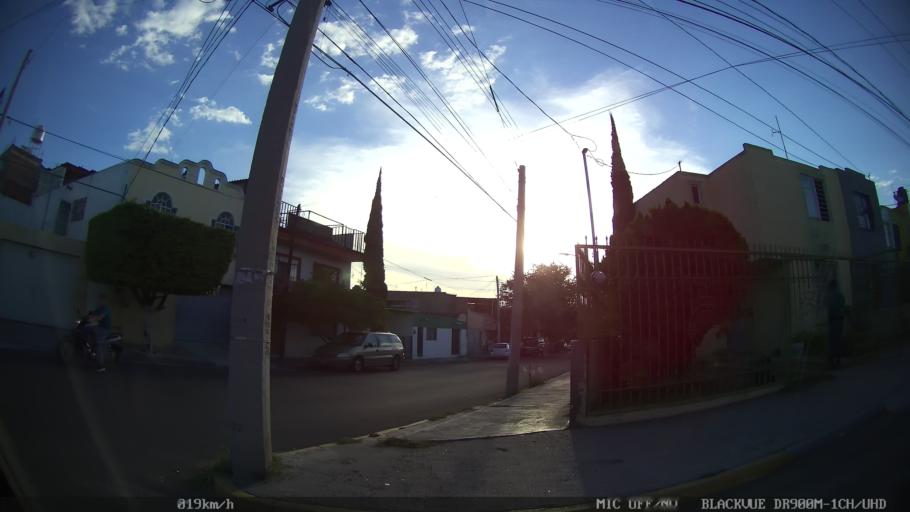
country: MX
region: Jalisco
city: Tlaquepaque
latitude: 20.7088
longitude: -103.3002
